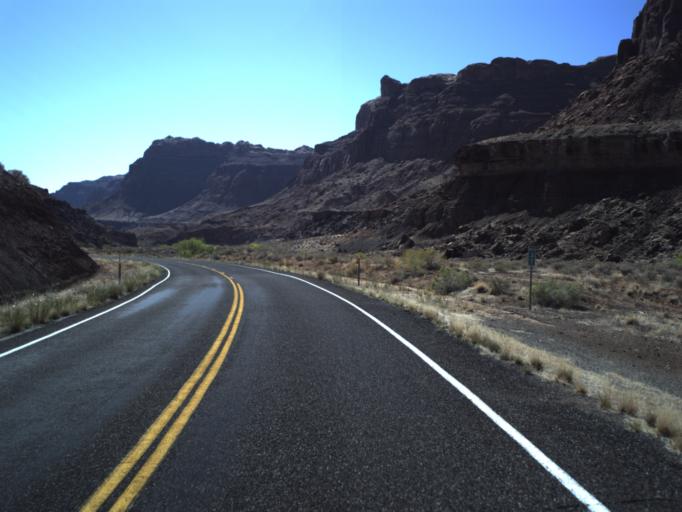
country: US
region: Utah
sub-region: San Juan County
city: Blanding
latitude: 37.9190
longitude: -110.4632
